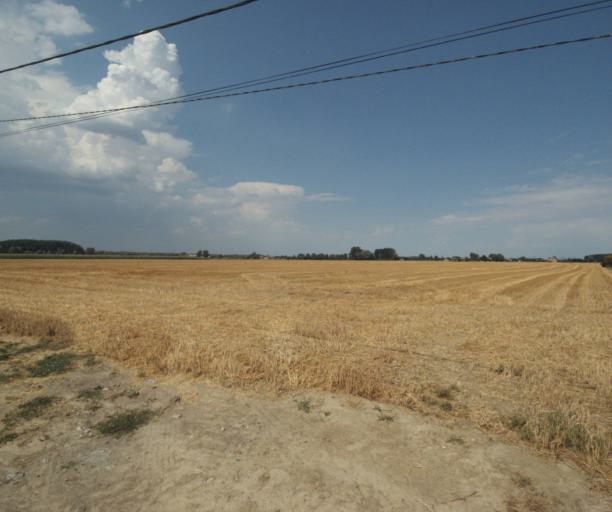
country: FR
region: Nord-Pas-de-Calais
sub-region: Departement du Nord
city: Deulemont
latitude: 50.7399
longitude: 2.9795
